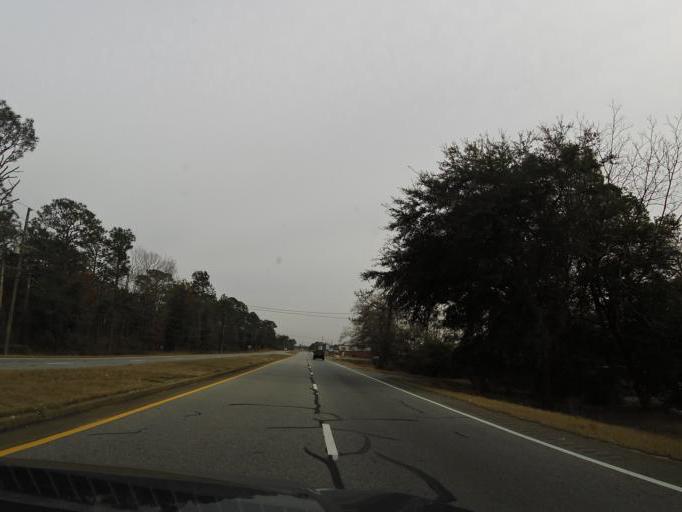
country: US
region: Georgia
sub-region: Decatur County
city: Bainbridge
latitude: 30.9308
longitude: -84.6356
